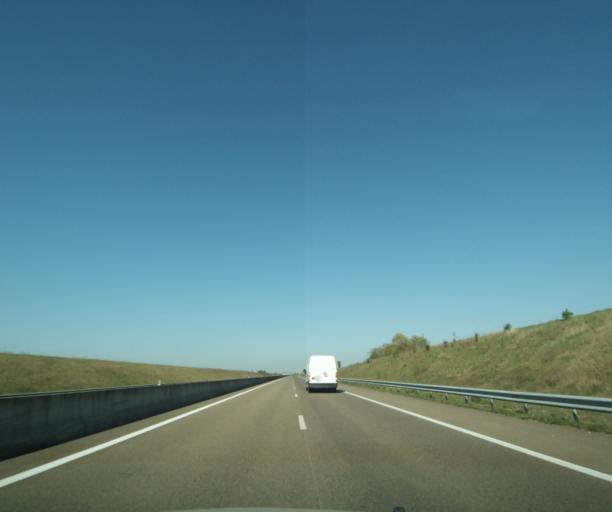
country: FR
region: Centre
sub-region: Departement du Loiret
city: Dadonville
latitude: 48.1114
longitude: 2.2933
